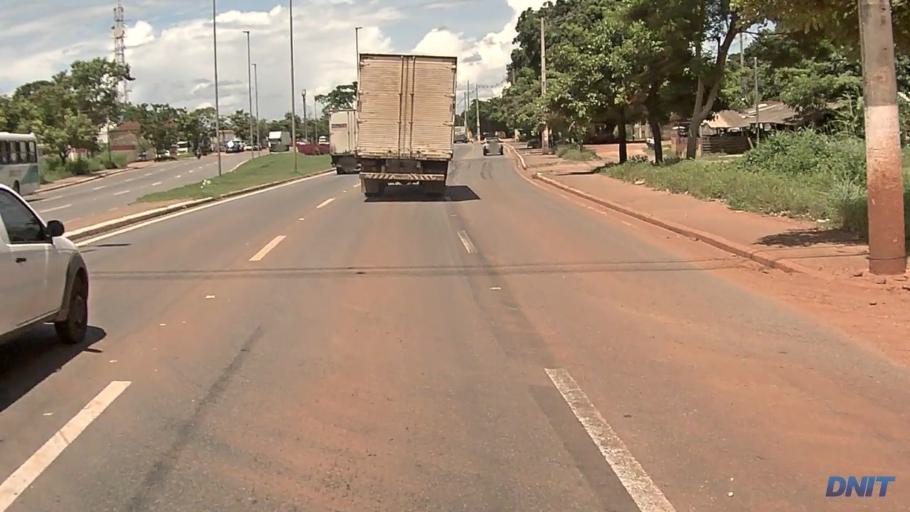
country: BR
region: Mato Grosso
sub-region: Cuiaba
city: Cuiaba
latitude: -15.6448
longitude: -56.0126
